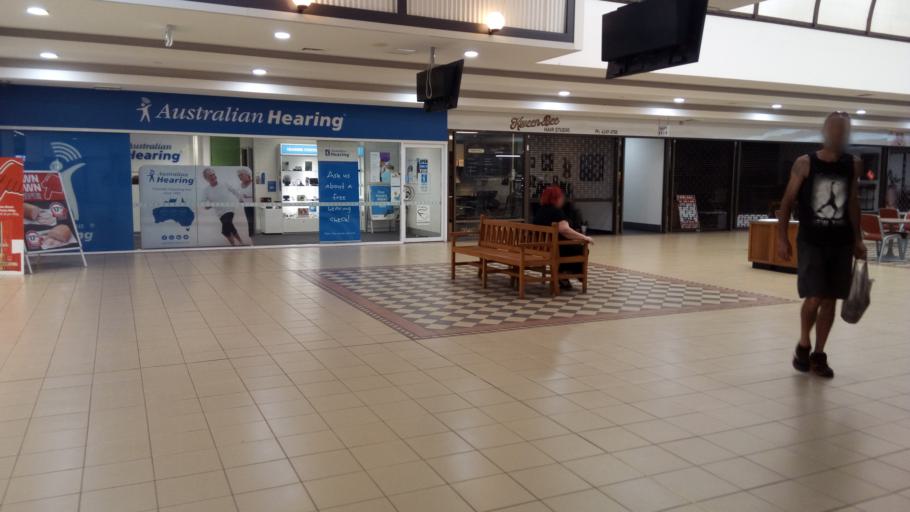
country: AU
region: New South Wales
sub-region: Wollongong
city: Corrimal
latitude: -34.3714
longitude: 150.8983
